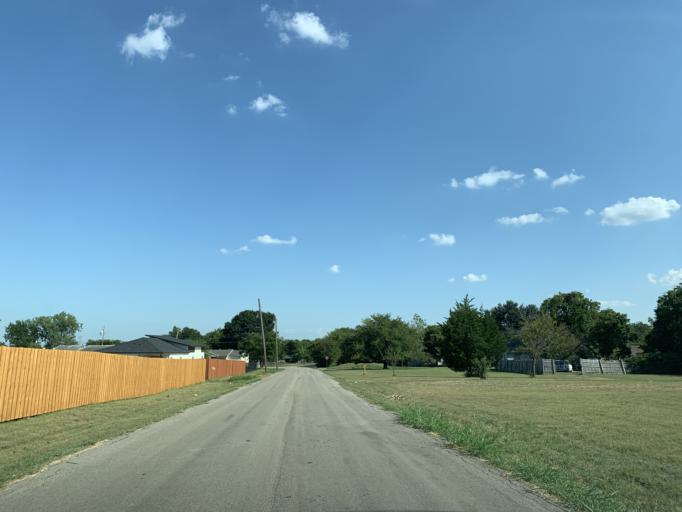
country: US
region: Texas
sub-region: Dallas County
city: Hutchins
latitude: 32.6579
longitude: -96.7710
